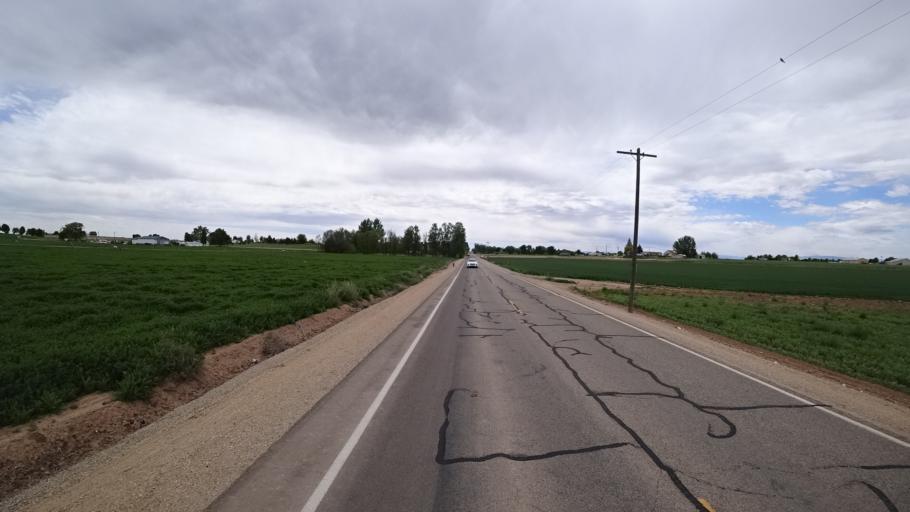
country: US
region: Idaho
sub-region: Ada County
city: Meridian
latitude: 43.5638
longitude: -116.4138
